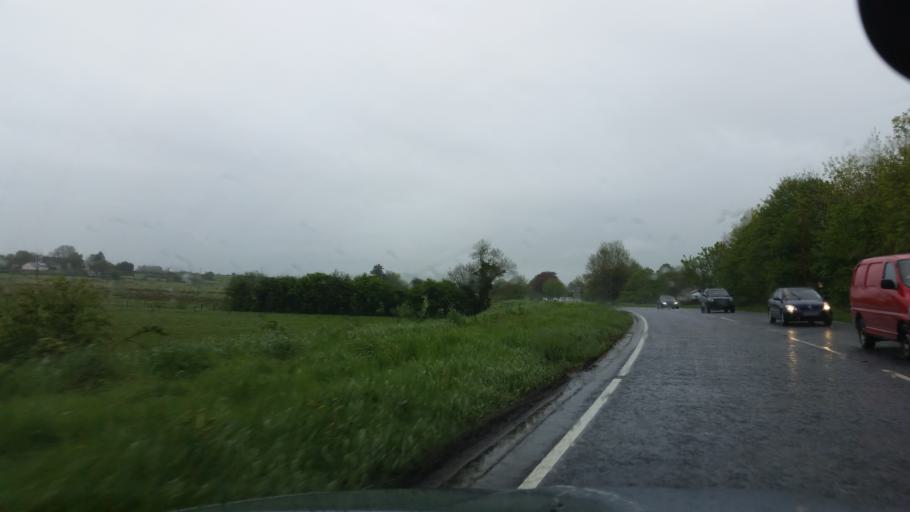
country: GB
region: Northern Ireland
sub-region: Strabane District
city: Strabane
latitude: 54.8437
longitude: -7.4474
